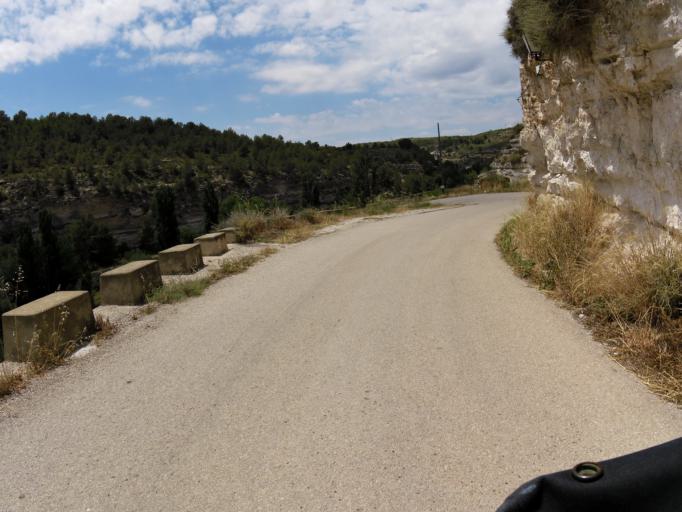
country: ES
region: Castille-La Mancha
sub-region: Provincia de Albacete
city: Valdeganga
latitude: 39.1606
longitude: -1.6095
